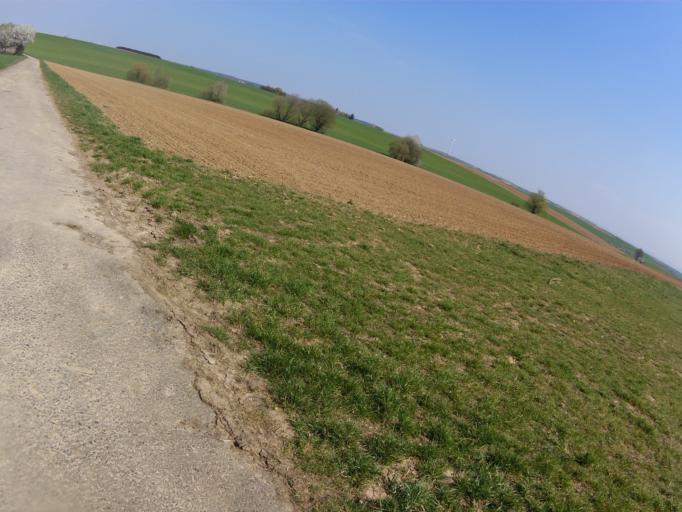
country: DE
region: Bavaria
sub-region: Regierungsbezirk Unterfranken
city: Mainstockheim
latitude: 49.8100
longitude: 10.1124
